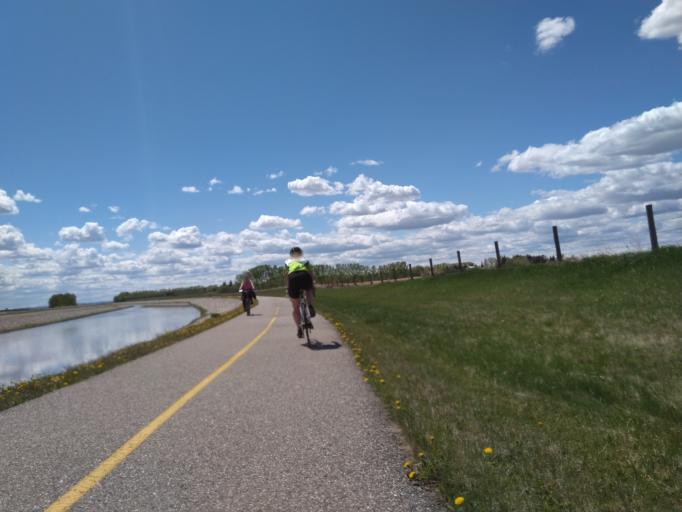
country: CA
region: Alberta
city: Chestermere
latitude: 51.0029
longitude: -113.8571
